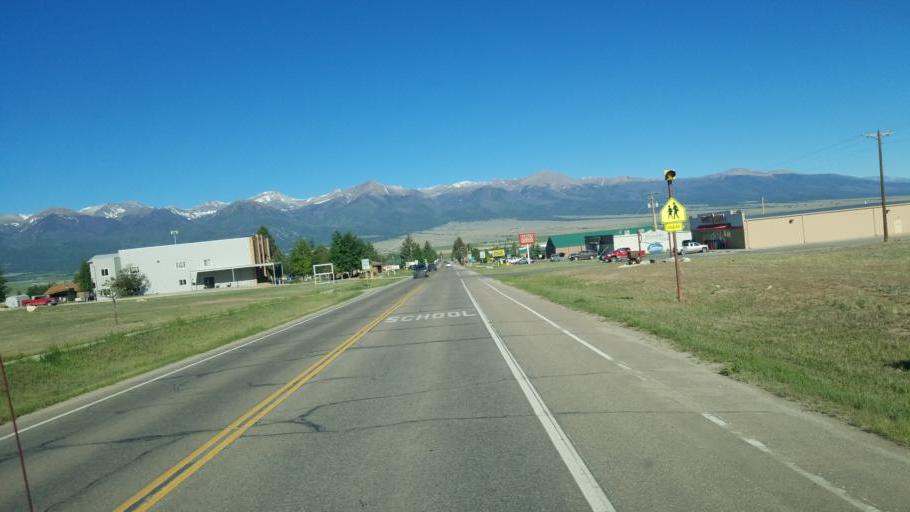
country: US
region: Colorado
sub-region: Custer County
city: Westcliffe
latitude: 38.1358
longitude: -105.4559
